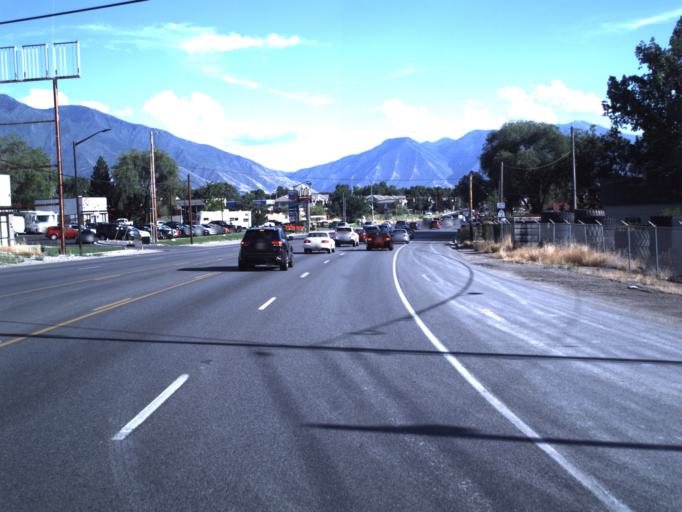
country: US
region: Utah
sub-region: Utah County
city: Springville
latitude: 40.1879
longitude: -111.6110
